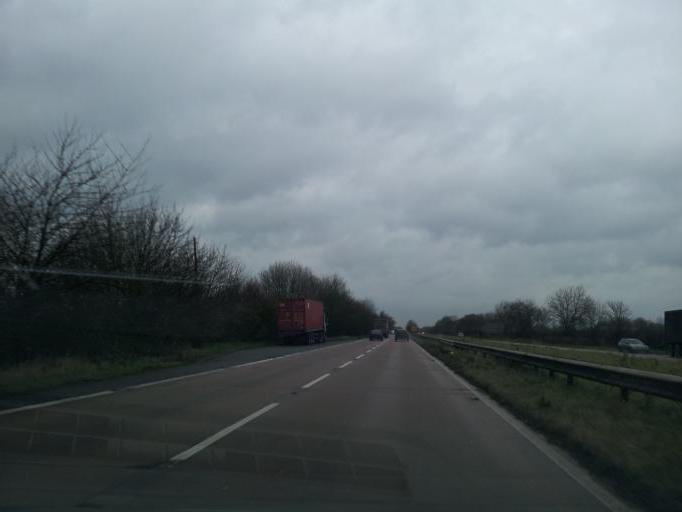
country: GB
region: England
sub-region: Leicestershire
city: Grimston
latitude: 52.7860
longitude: -1.0458
